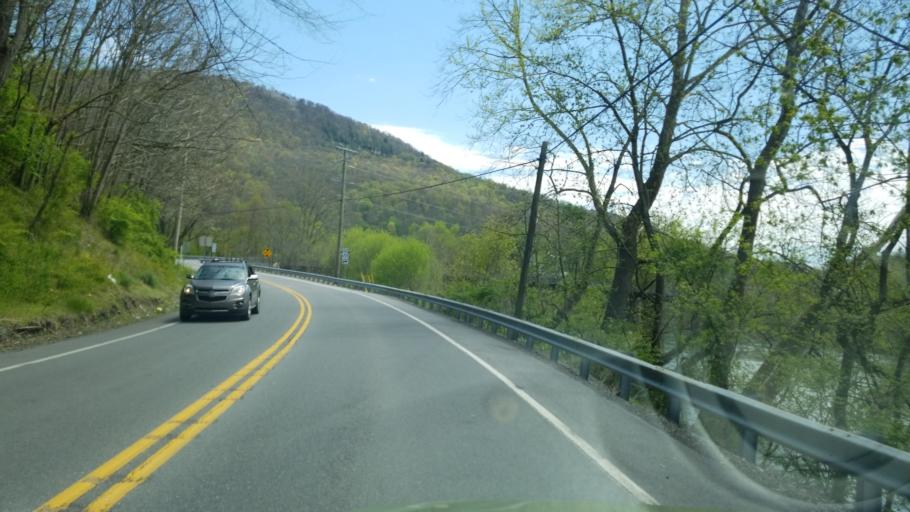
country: US
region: Pennsylvania
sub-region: Huntingdon County
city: Mount Union
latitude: 40.3961
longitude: -77.9396
